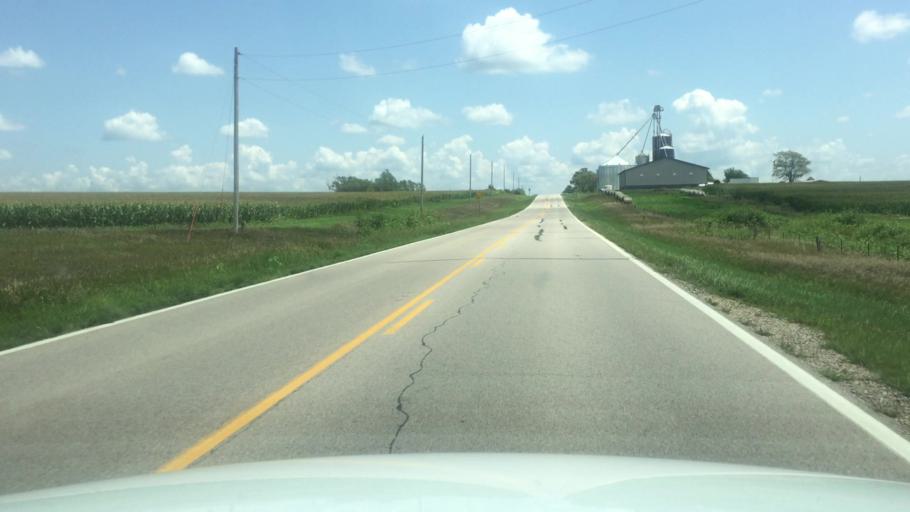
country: US
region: Kansas
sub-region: Brown County
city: Horton
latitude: 39.6673
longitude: -95.6081
